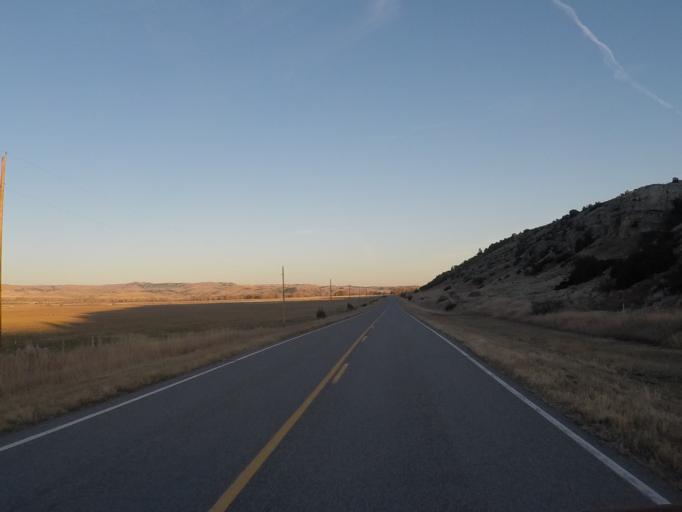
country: US
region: Montana
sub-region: Sweet Grass County
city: Big Timber
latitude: 45.7828
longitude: -109.8298
